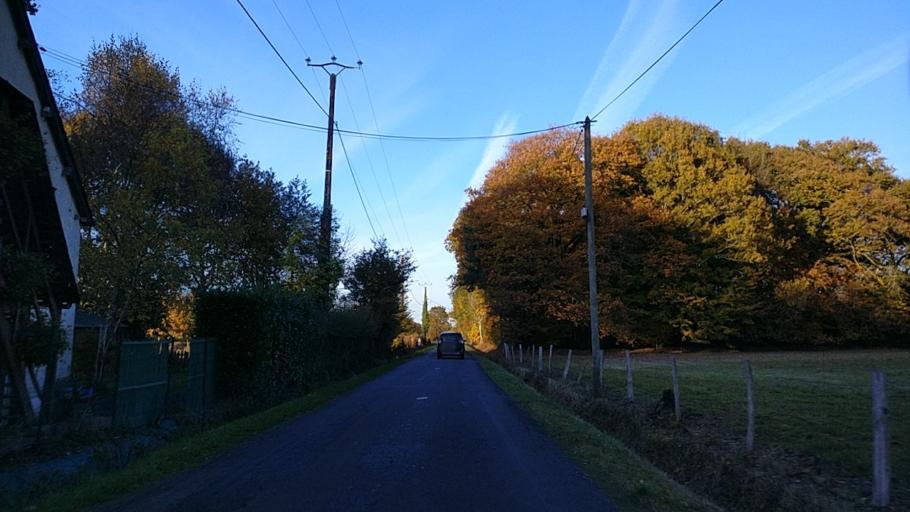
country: FR
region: Brittany
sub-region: Departement d'Ille-et-Vilaine
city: Saint-Sulpice-la-Foret
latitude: 48.2003
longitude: -1.5772
